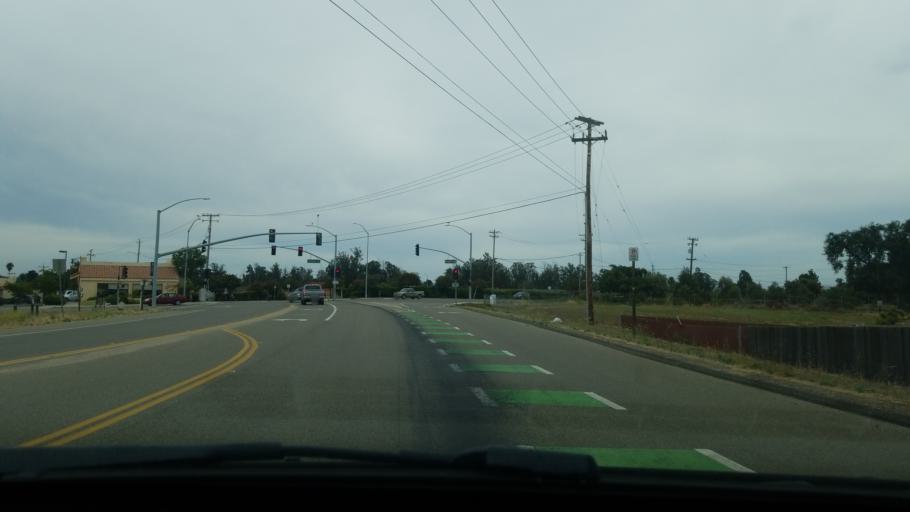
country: US
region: California
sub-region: San Luis Obispo County
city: Nipomo
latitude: 35.0227
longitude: -120.4892
